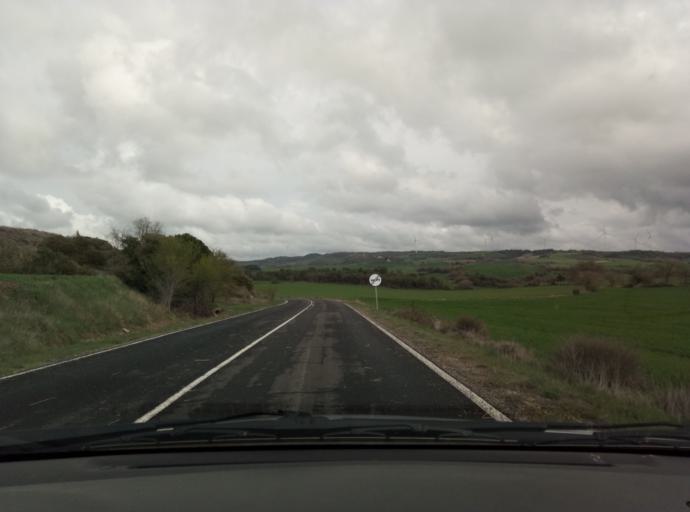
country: ES
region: Catalonia
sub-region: Provincia de Tarragona
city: Santa Coloma de Queralt
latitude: 41.5727
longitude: 1.3396
